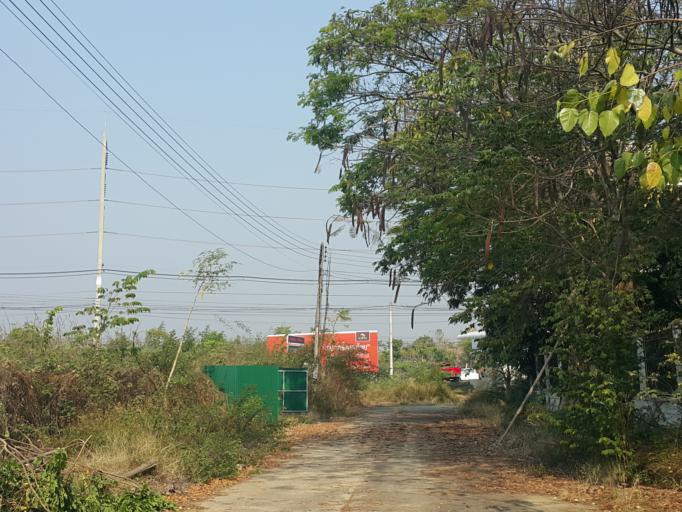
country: TH
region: Chiang Mai
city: San Kamphaeng
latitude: 18.7777
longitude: 99.0707
